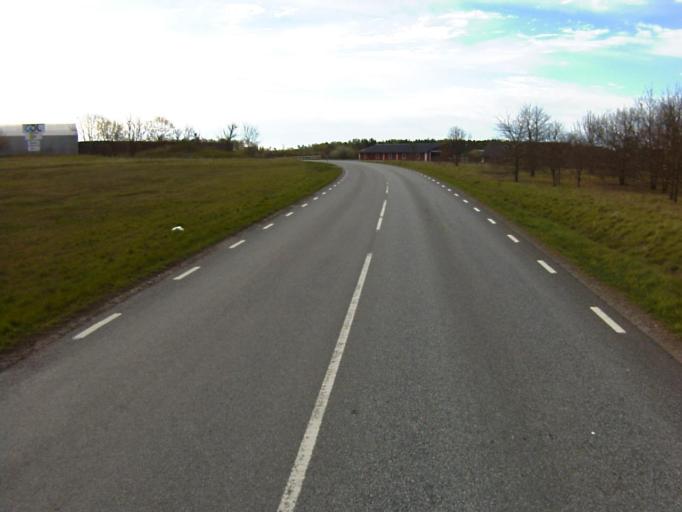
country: SE
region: Skane
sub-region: Kristianstads Kommun
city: Norra Asum
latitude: 55.9951
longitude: 14.1140
